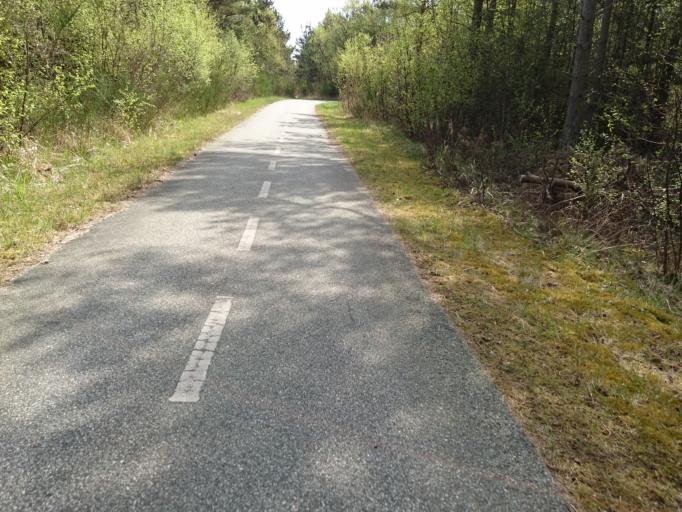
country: DK
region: North Denmark
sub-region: Frederikshavn Kommune
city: Skagen
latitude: 57.6424
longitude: 10.4611
